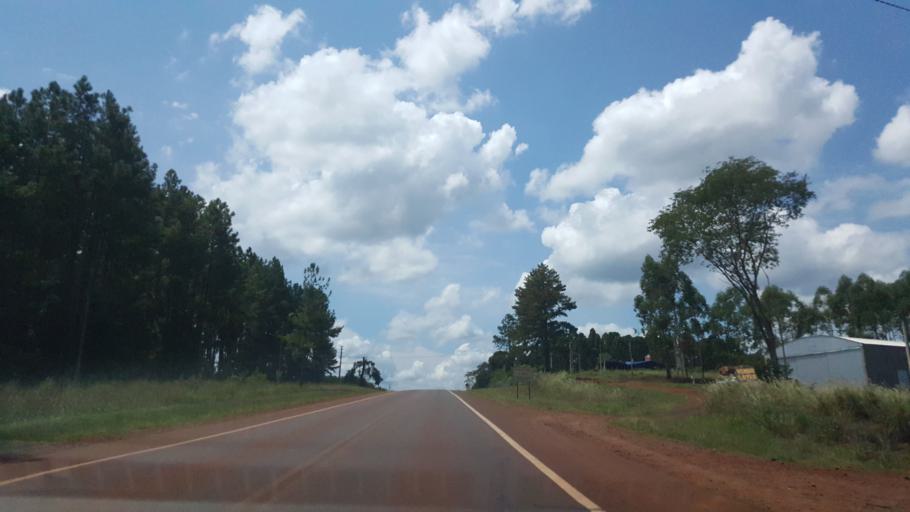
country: AR
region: Misiones
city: Garuhape
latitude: -26.8149
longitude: -54.9451
